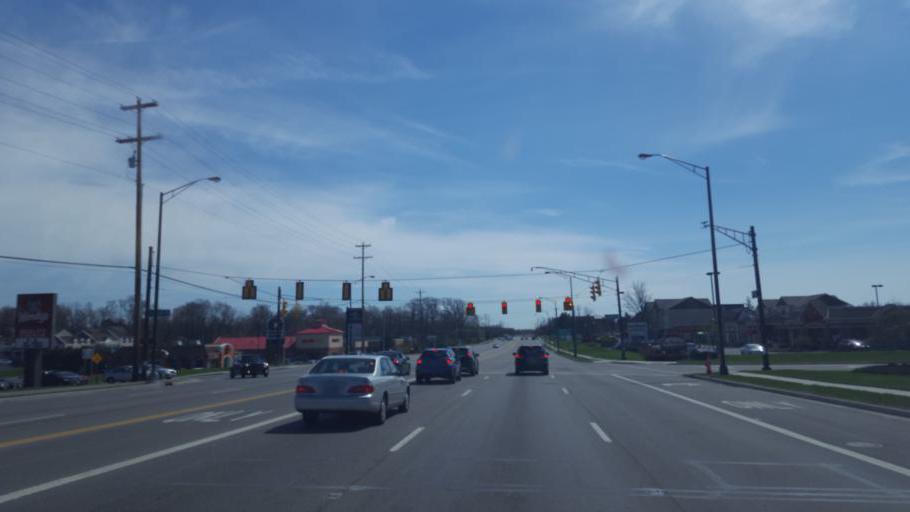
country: US
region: Ohio
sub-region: Franklin County
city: Worthington
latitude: 40.1361
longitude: -83.0171
